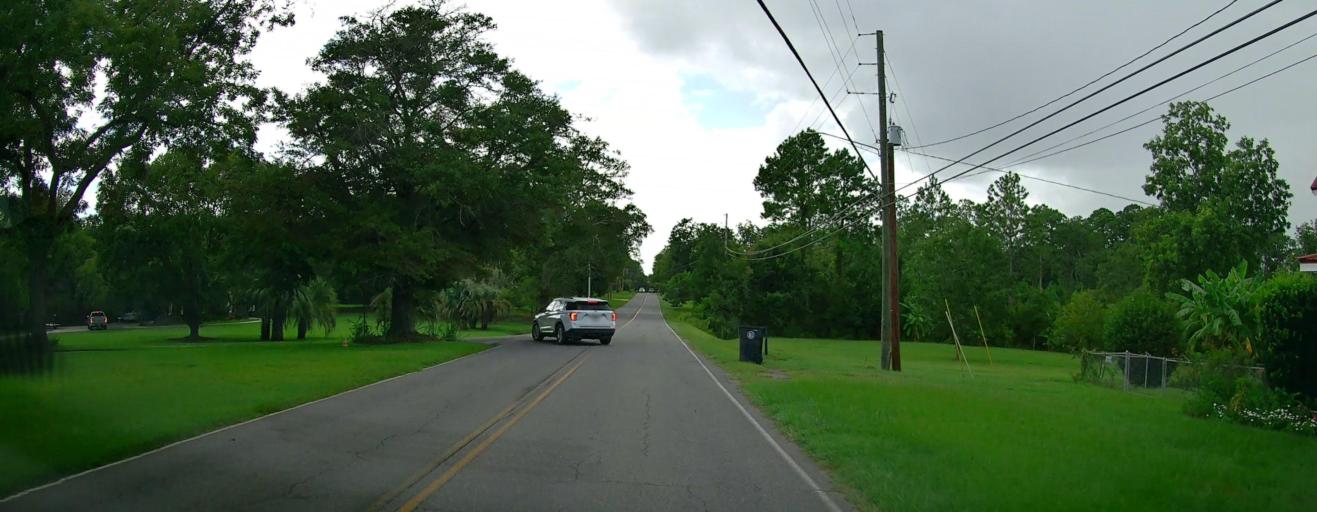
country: US
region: Georgia
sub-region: Ben Hill County
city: Fitzgerald
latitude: 31.7053
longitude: -83.2690
